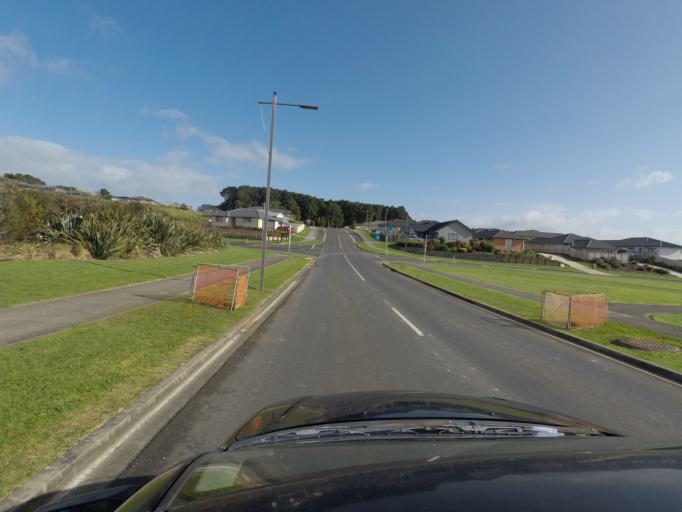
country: NZ
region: Northland
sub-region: Whangarei
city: Whangarei
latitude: -35.6778
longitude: 174.3167
